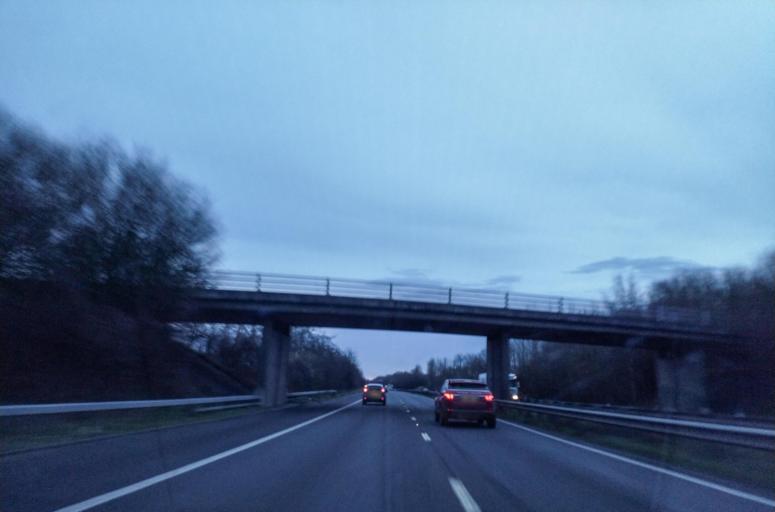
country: GB
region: England
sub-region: Kent
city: Sittingbourne
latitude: 51.3080
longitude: 0.7142
